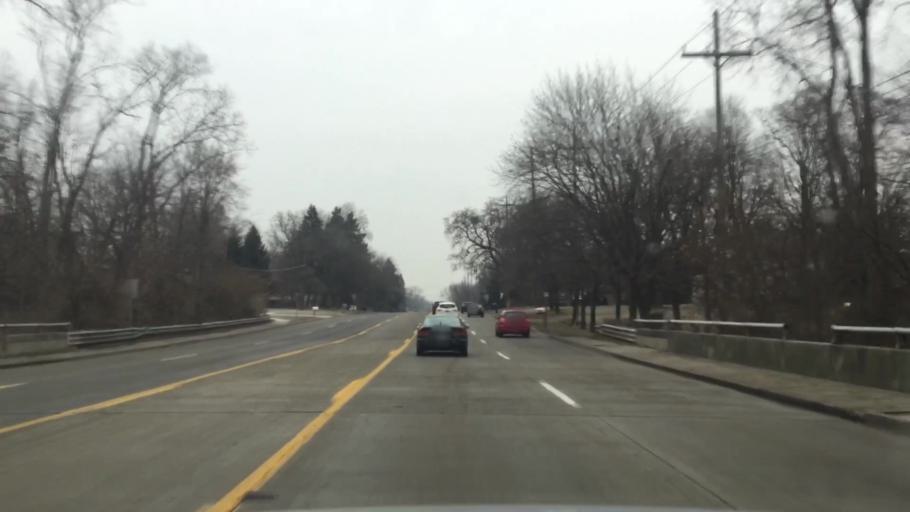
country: US
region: Michigan
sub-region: Oakland County
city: Farmington
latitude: 42.4205
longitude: -83.3550
